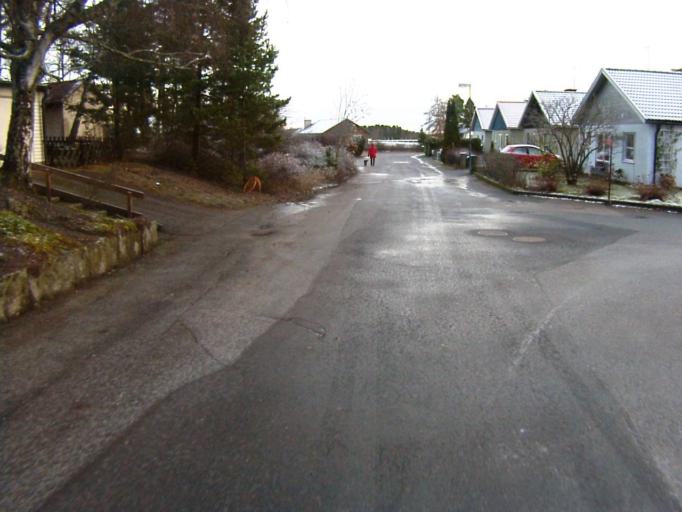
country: SE
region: Soedermanland
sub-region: Eskilstuna Kommun
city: Hallbybrunn
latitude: 59.3987
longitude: 16.4144
